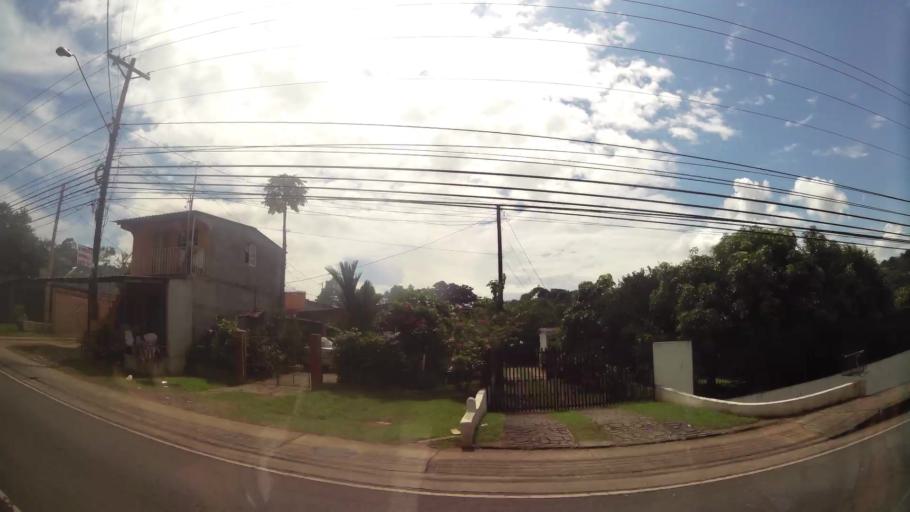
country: PA
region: Panama
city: Vista Alegre
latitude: 8.9336
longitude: -79.6916
